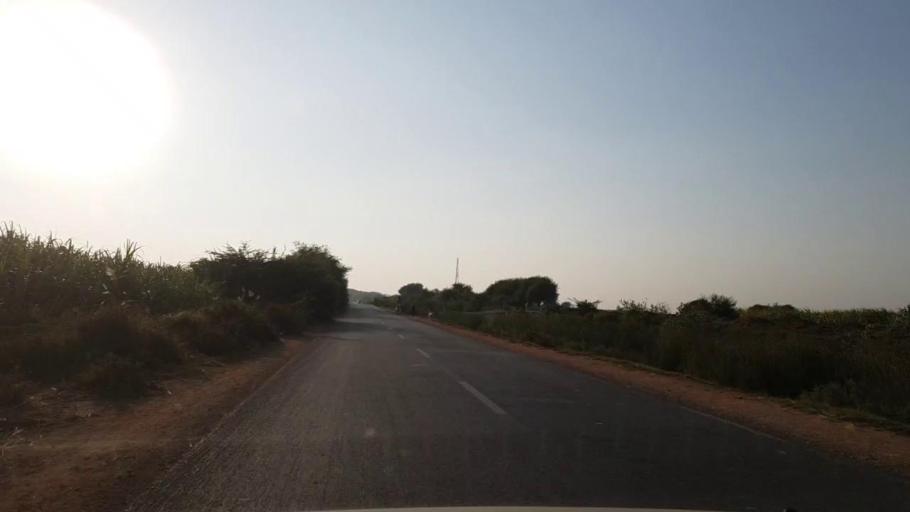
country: PK
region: Sindh
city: Mirpur Batoro
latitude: 24.6874
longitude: 68.1722
